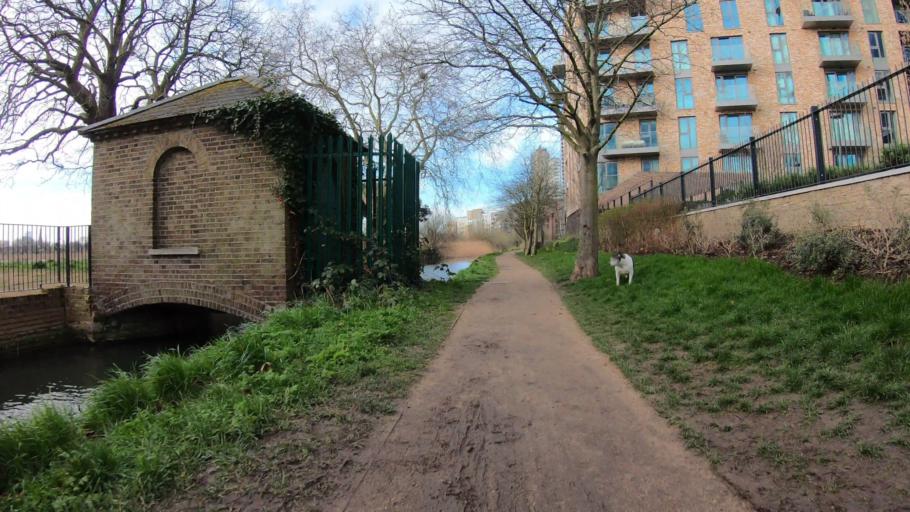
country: GB
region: England
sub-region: Greater London
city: Harringay
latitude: 51.5742
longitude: -0.0761
